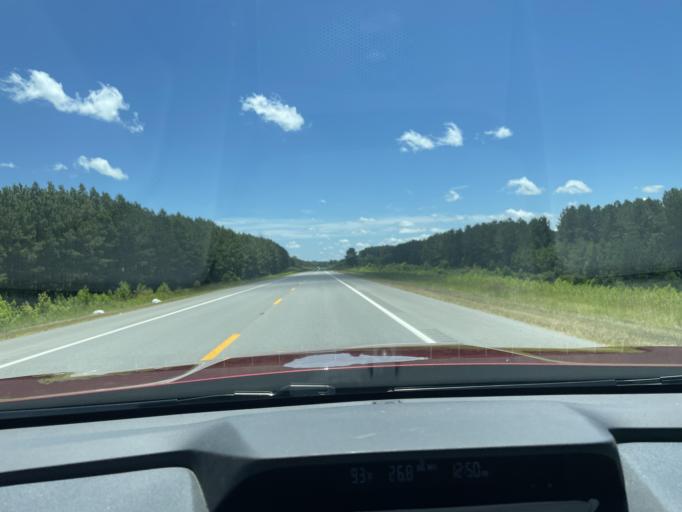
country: US
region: Arkansas
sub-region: Lincoln County
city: Star City
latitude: 33.9523
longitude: -91.9031
